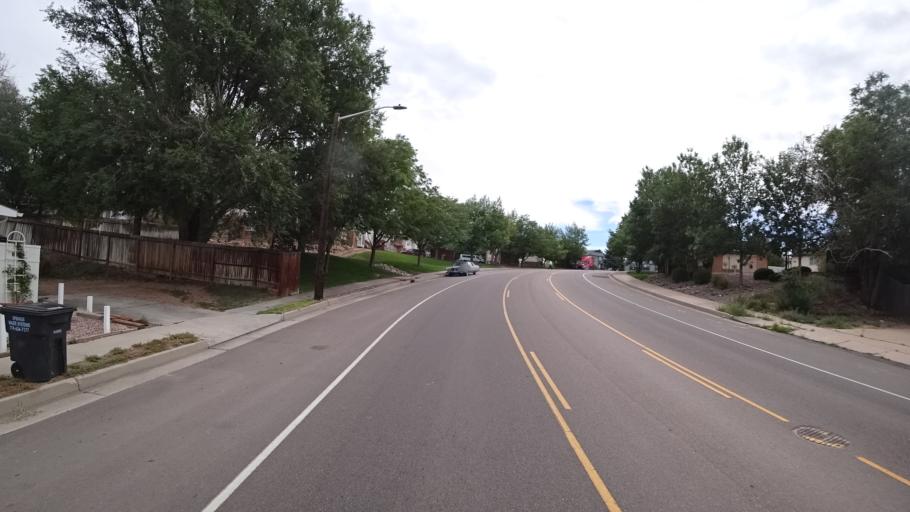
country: US
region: Colorado
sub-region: El Paso County
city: Fountain
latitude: 38.6972
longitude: -104.7006
